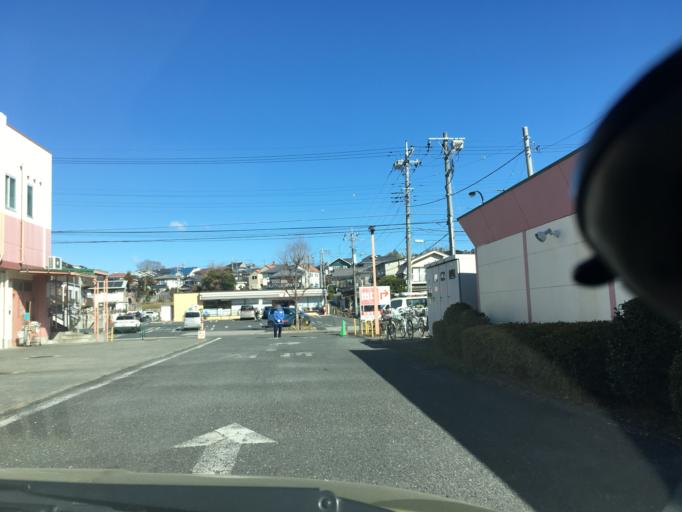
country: JP
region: Tokyo
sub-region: Machida-shi
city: Machida
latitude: 35.5859
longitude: 139.3932
